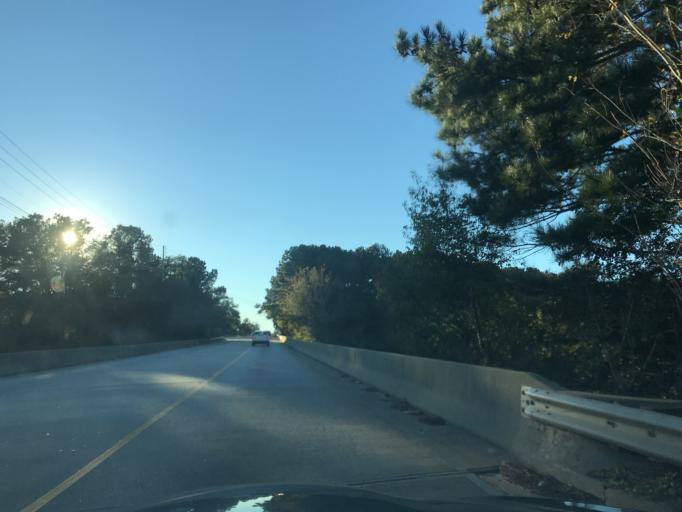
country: US
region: North Carolina
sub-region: Wake County
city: Garner
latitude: 35.7476
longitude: -78.5929
